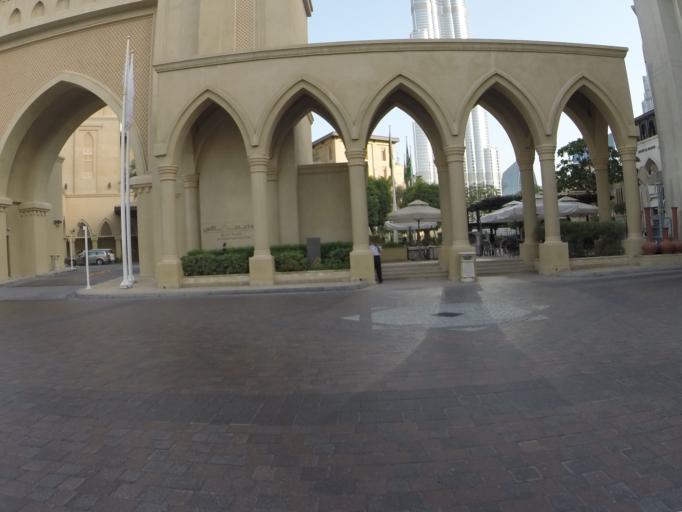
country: AE
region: Dubai
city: Dubai
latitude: 25.1933
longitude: 55.2765
